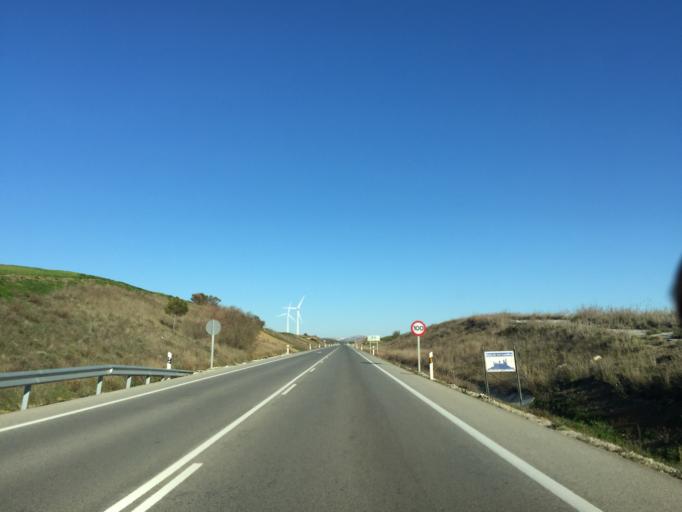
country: ES
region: Andalusia
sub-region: Provincia de Malaga
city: Ardales
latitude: 36.9234
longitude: -4.8465
